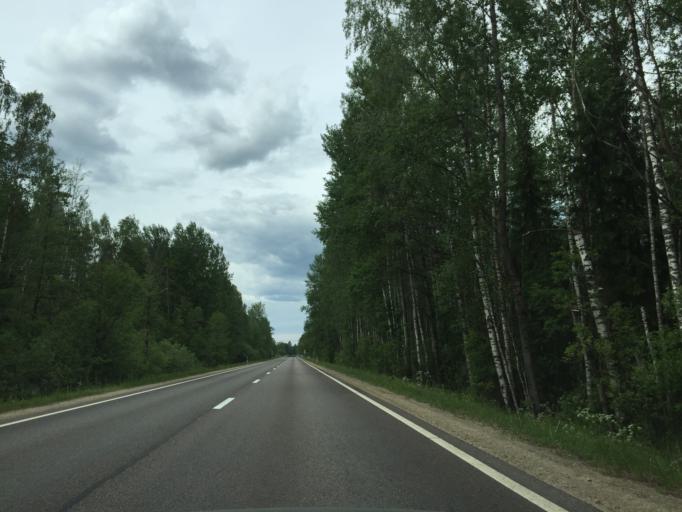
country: LV
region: Livani
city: Livani
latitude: 56.5398
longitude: 26.1292
